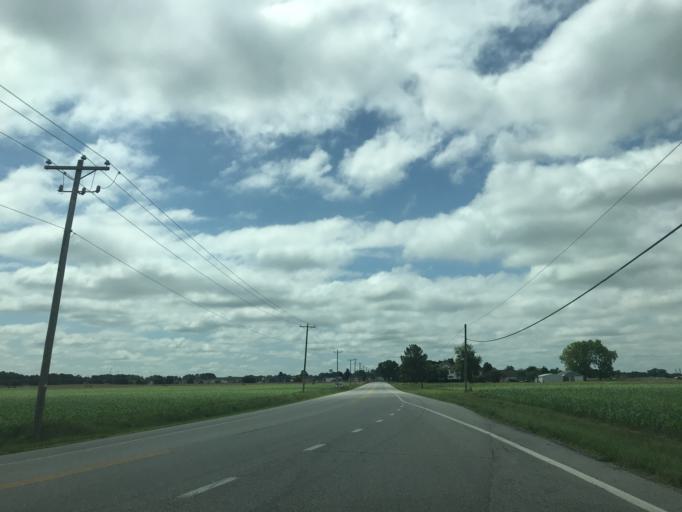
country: US
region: Maryland
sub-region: Caroline County
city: Ridgely
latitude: 38.9595
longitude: -75.8903
